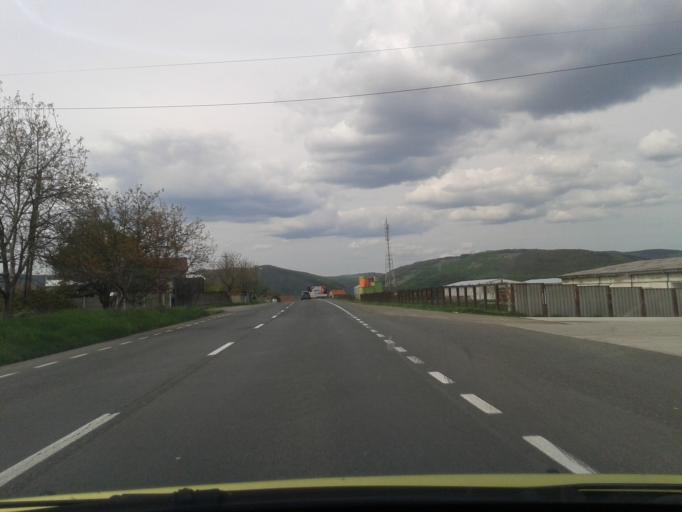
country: RO
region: Hunedoara
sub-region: Comuna Soimus
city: Soimus
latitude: 45.9107
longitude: 22.8628
